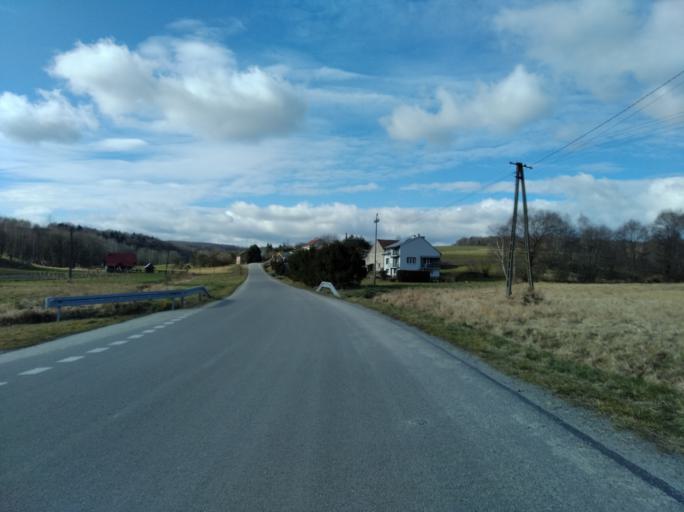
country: PL
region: Subcarpathian Voivodeship
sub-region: Powiat strzyzowski
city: Wisniowa
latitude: 49.9131
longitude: 21.6764
